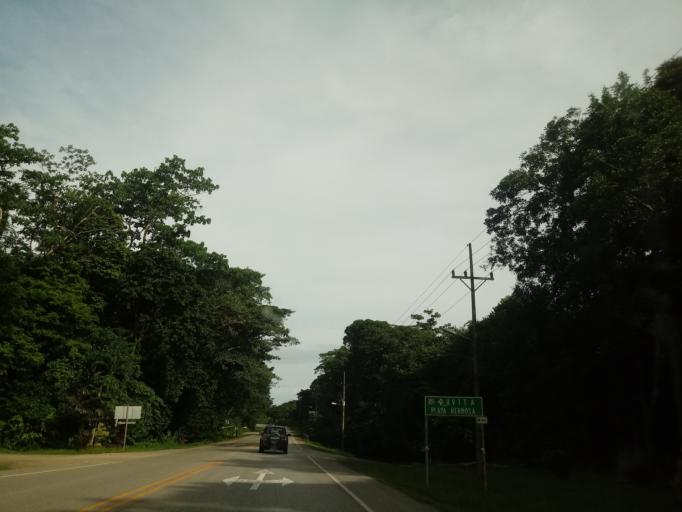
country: CR
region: San Jose
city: Daniel Flores
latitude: 9.1991
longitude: -83.7840
